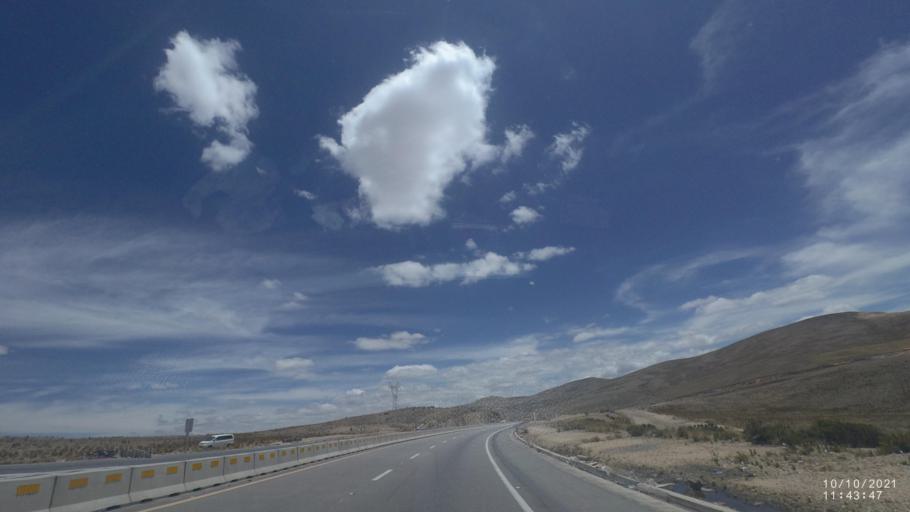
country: BO
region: Cochabamba
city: Colchani
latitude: -17.6729
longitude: -66.7570
